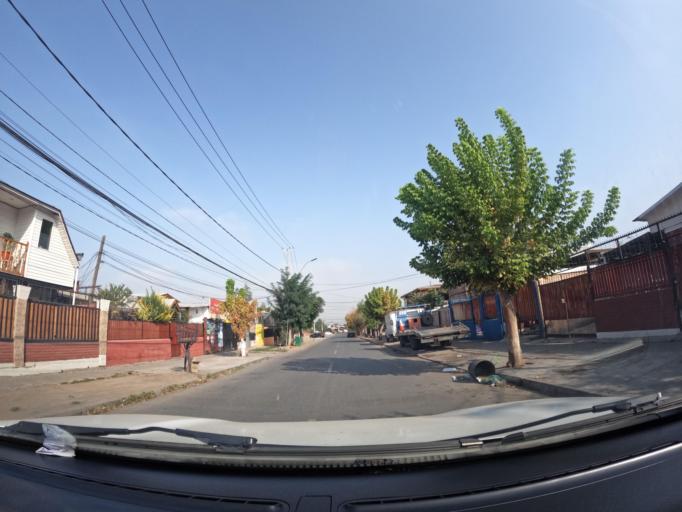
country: CL
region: Santiago Metropolitan
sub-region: Provincia de Santiago
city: Villa Presidente Frei, Nunoa, Santiago, Chile
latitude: -33.4734
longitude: -70.5641
